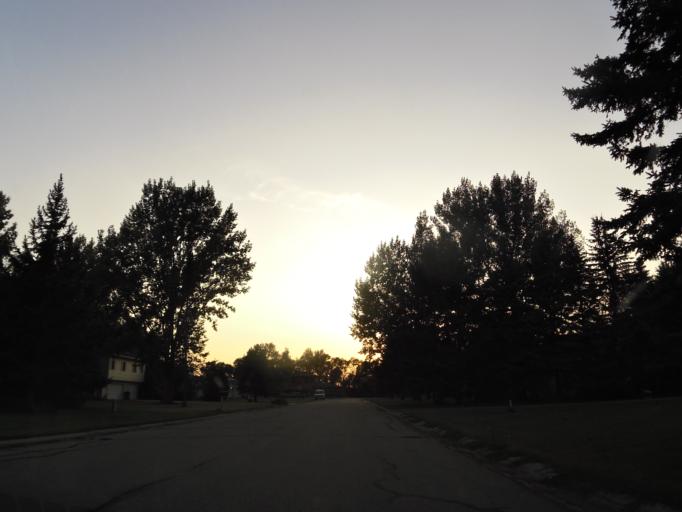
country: US
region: North Dakota
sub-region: Grand Forks County
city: Grand Forks
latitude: 47.8536
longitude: -97.0096
